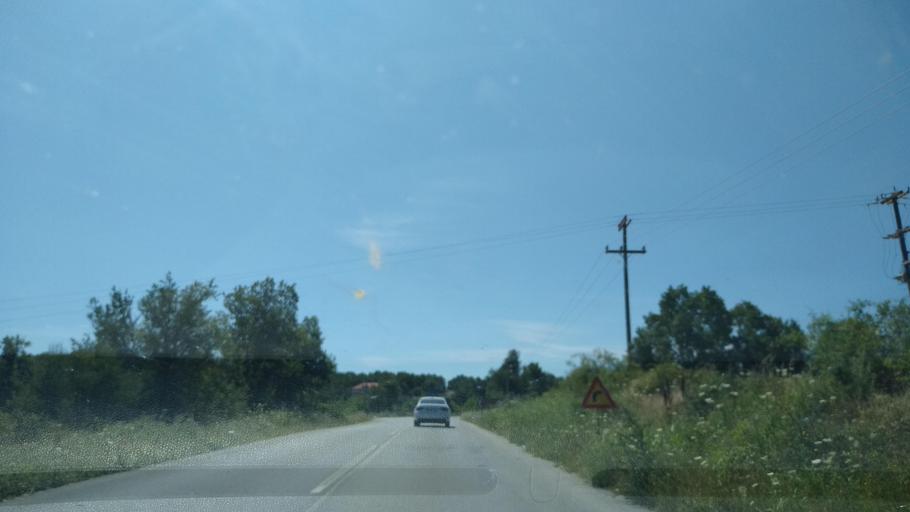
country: GR
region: Central Macedonia
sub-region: Nomos Chalkidikis
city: Megali Panagia
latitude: 40.4160
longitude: 23.6926
